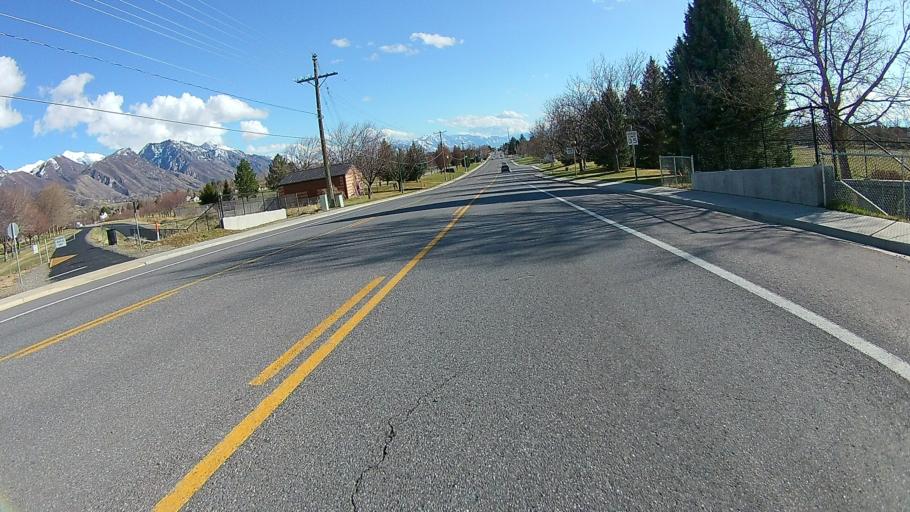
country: US
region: Utah
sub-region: Utah County
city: Orem
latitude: 40.3232
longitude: -111.6769
